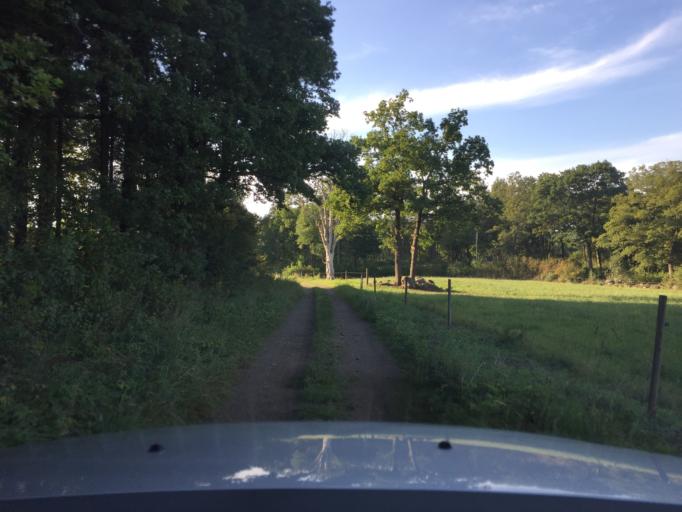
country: SE
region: Skane
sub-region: Hassleholms Kommun
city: Sosdala
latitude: 56.0217
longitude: 13.7108
